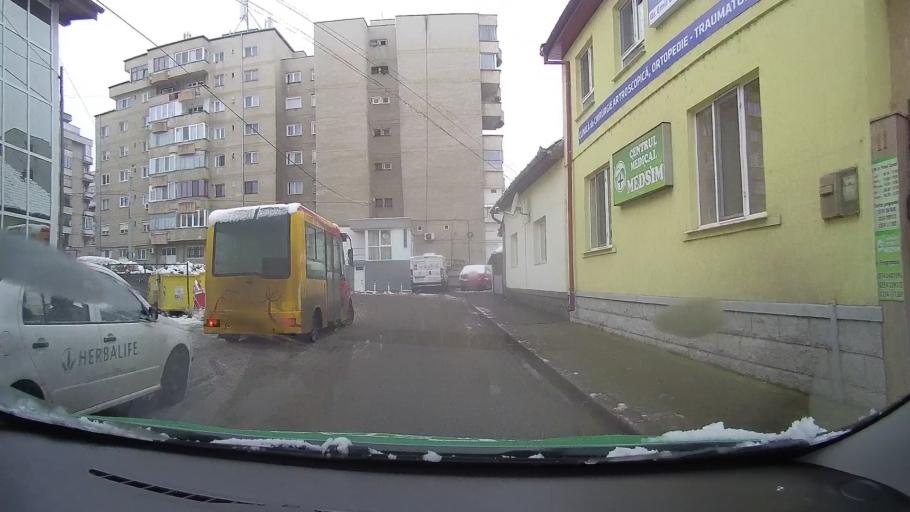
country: RO
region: Hunedoara
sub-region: Municipiul Deva
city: Deva
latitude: 45.8767
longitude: 22.9084
